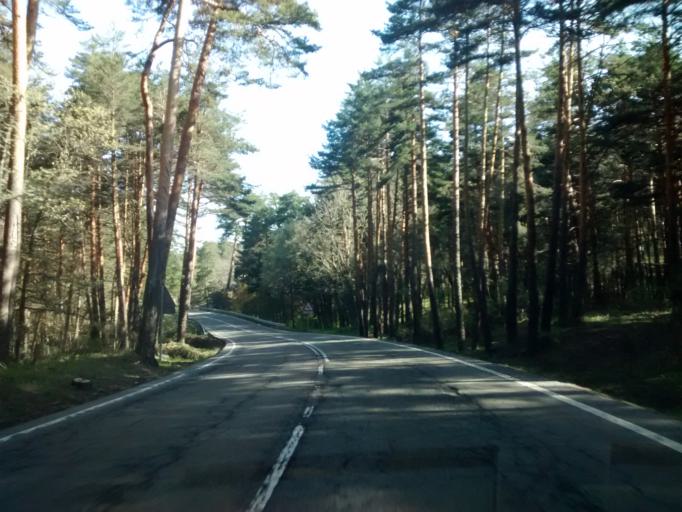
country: ES
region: Castille and Leon
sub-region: Provincia de Segovia
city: San Ildefonso
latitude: 40.8374
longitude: -4.0250
